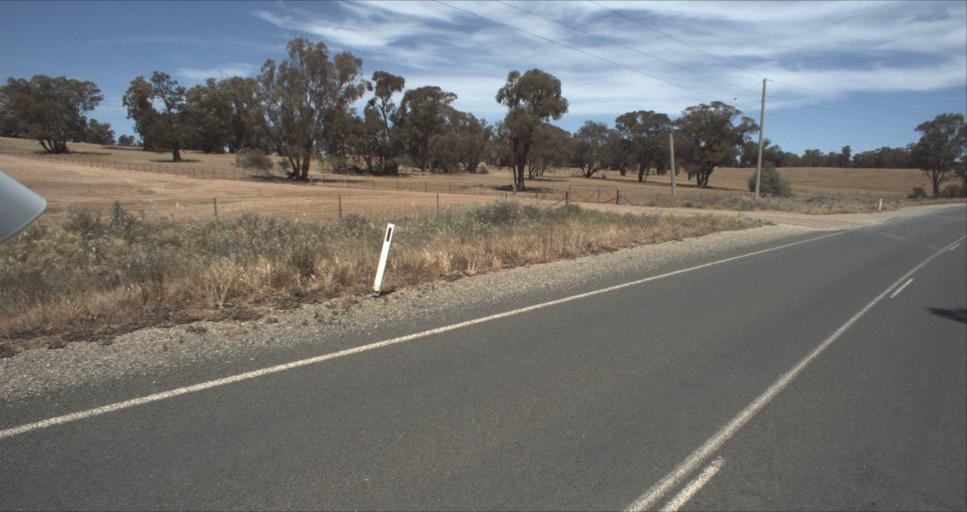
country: AU
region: New South Wales
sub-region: Leeton
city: Leeton
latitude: -34.6579
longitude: 146.4576
